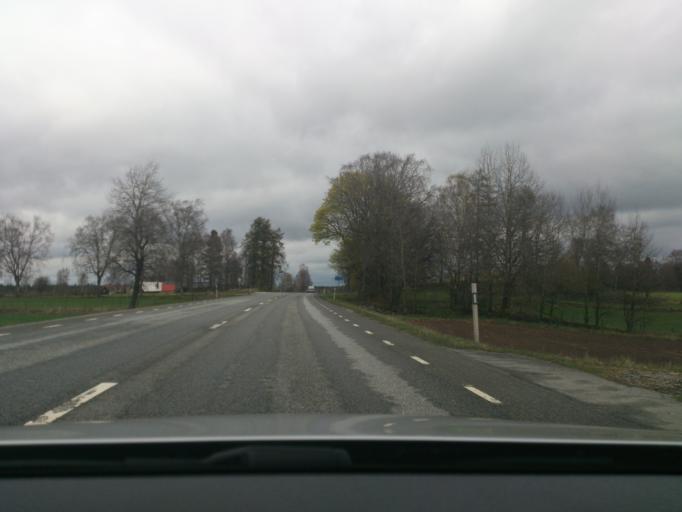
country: SE
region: Vaestra Goetaland
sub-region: Ulricehamns Kommun
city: Ulricehamn
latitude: 57.9625
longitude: 13.5250
